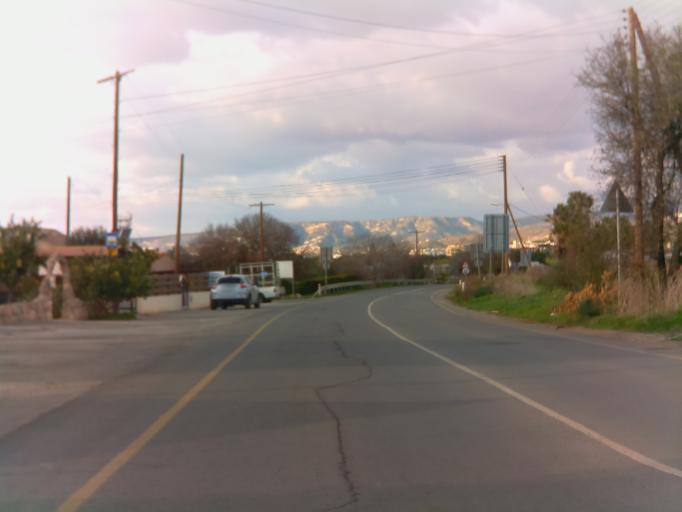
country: CY
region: Pafos
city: Chlorakas
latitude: 34.8105
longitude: 32.4104
